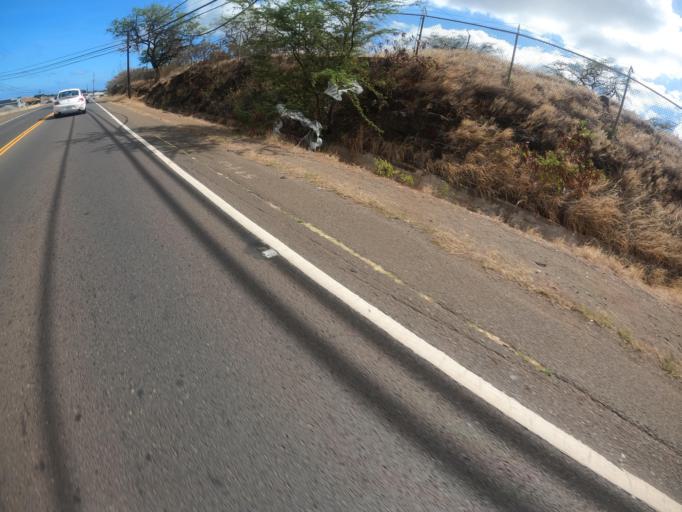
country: US
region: Hawaii
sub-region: Honolulu County
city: Makakilo City
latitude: 21.3379
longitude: -158.0743
